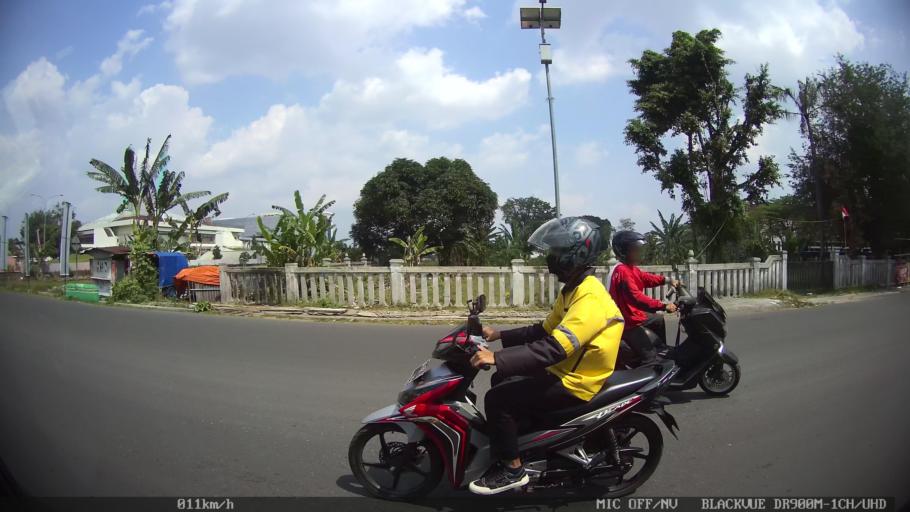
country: ID
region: Daerah Istimewa Yogyakarta
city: Depok
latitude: -7.7985
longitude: 110.4058
